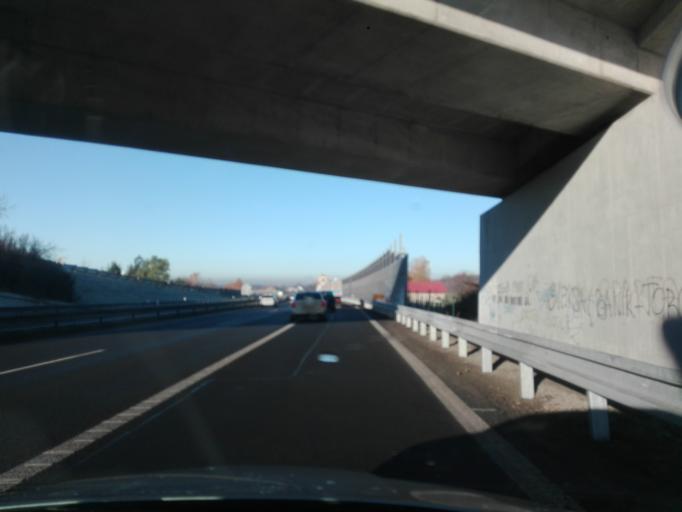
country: CZ
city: Dobra
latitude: 49.6747
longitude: 18.4258
